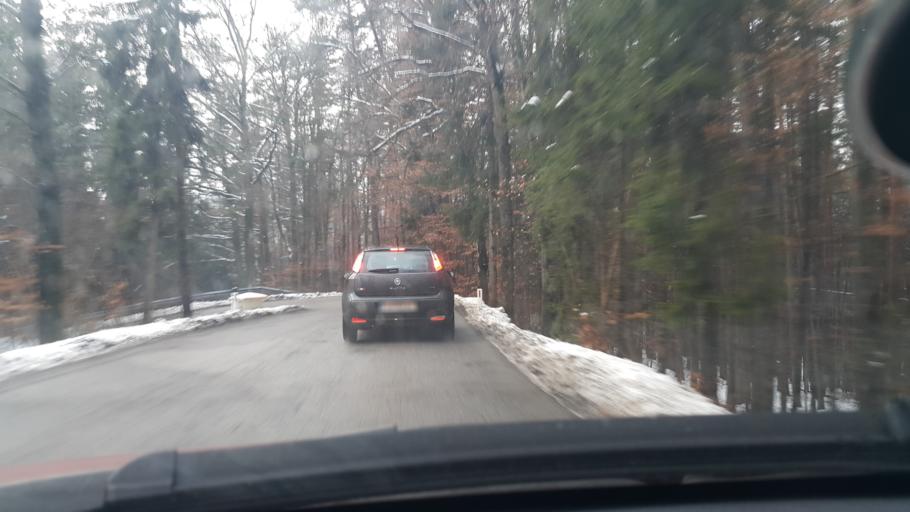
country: AT
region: Styria
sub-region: Politischer Bezirk Graz-Umgebung
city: Hitzendorf
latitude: 47.0640
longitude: 15.3056
